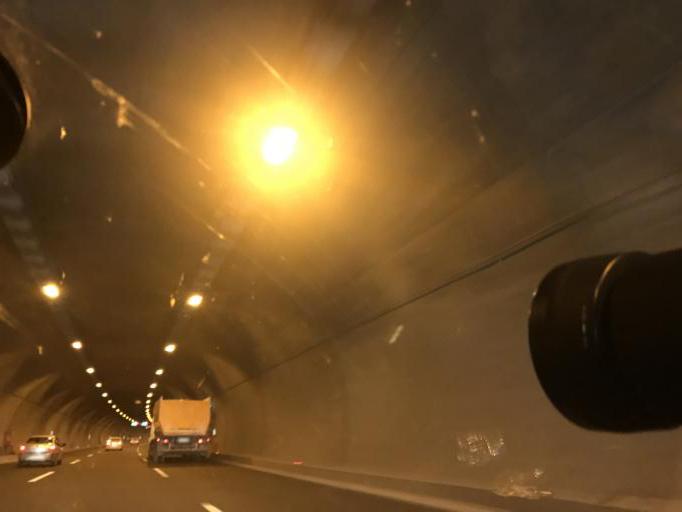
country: TR
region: Nigde
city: Ciftehan
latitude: 37.5088
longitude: 34.8193
